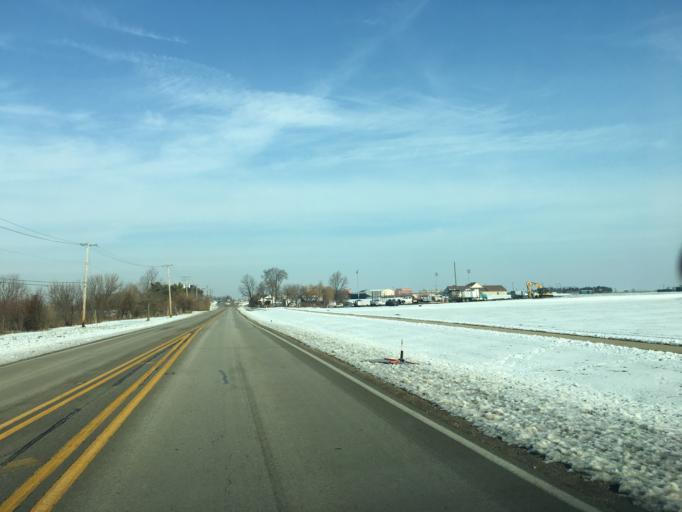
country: US
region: Illinois
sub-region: Will County
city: Plainfield
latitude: 41.6579
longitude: -88.1782
